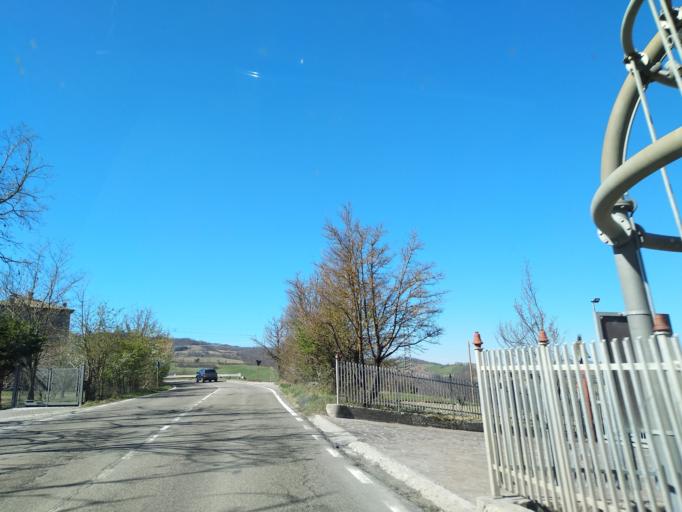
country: IT
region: Emilia-Romagna
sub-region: Provincia di Reggio Emilia
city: Castelnovo ne'Monti
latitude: 44.4271
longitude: 10.3834
